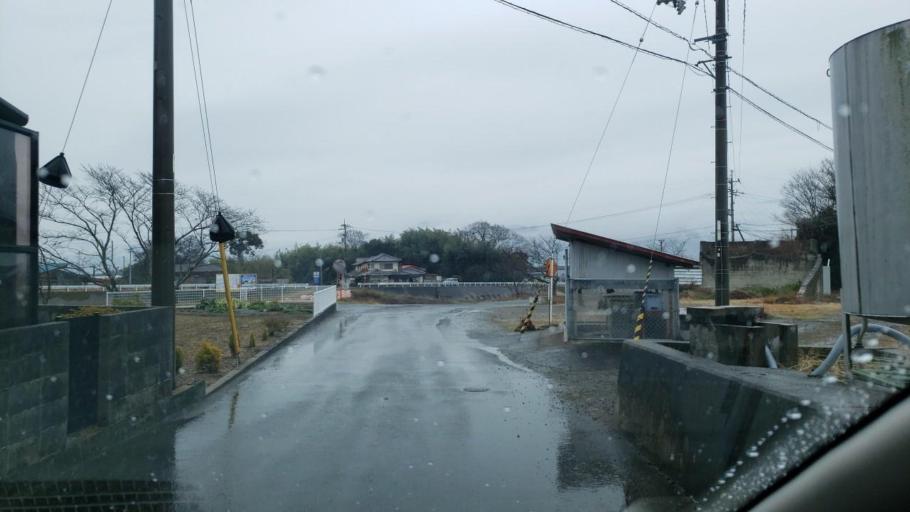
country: JP
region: Tokushima
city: Wakimachi
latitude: 34.0875
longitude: 134.2366
